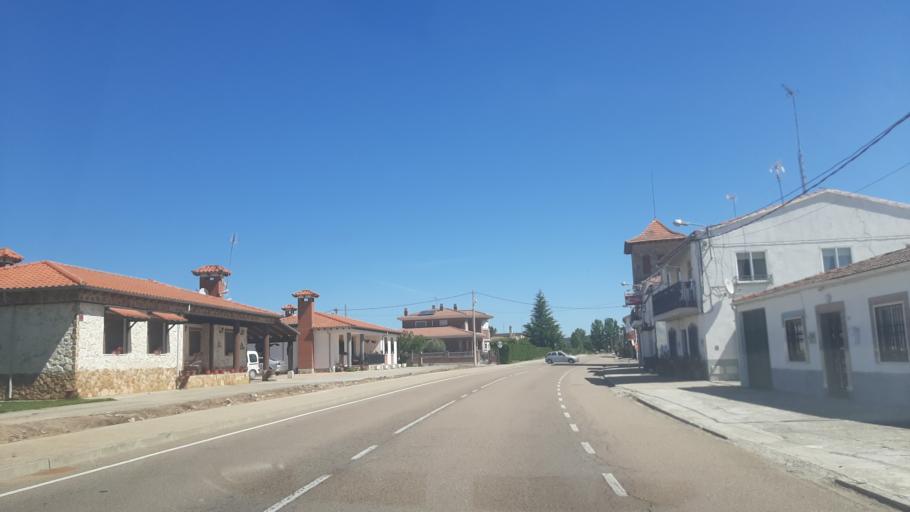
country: ES
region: Castille and Leon
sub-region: Provincia de Salamanca
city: Encinas de Arriba
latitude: 40.7709
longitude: -5.5579
